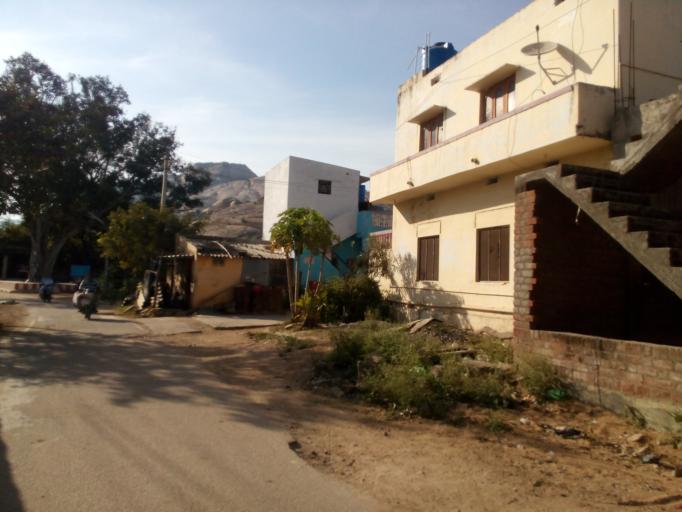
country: IN
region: Andhra Pradesh
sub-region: Chittoor
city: Narasingapuram
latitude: 13.5835
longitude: 79.3139
